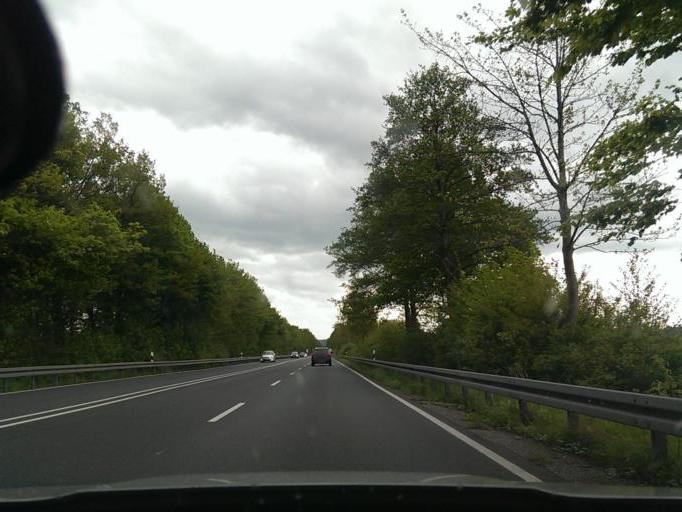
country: DE
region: Lower Saxony
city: Elze
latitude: 52.0981
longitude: 9.7433
